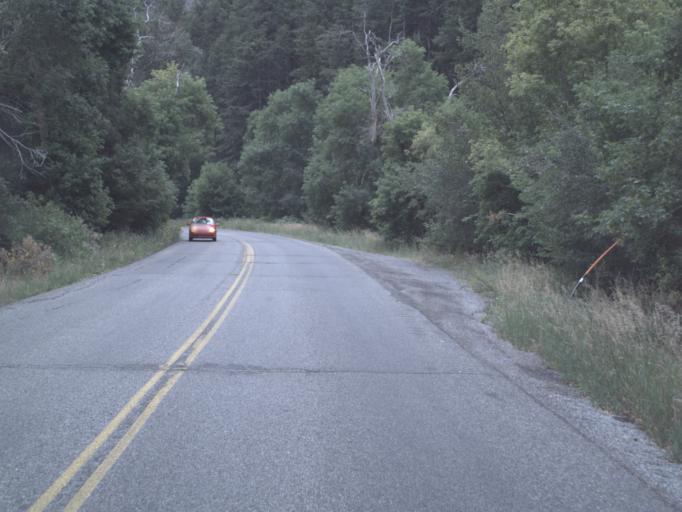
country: US
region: Utah
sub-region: Utah County
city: Orem
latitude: 40.3721
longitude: -111.5687
